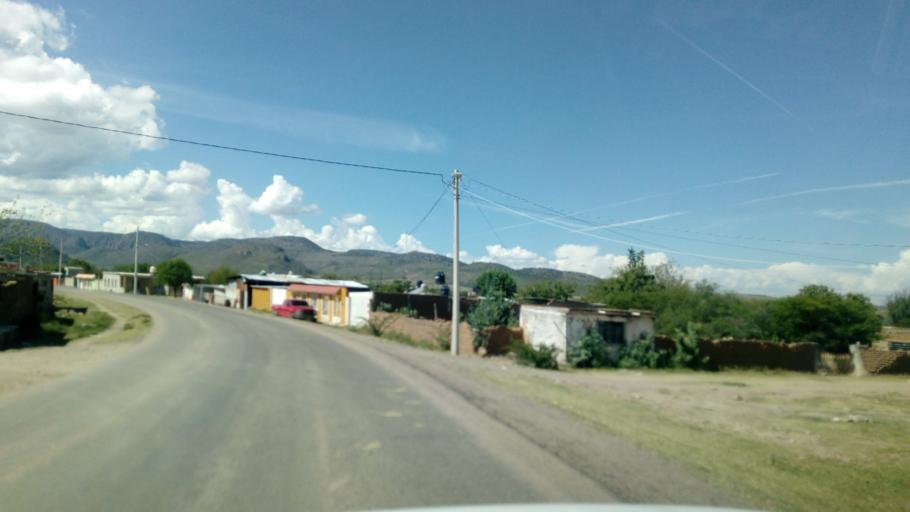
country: MX
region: Durango
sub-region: Durango
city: Jose Refugio Salcido
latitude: 23.8492
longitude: -104.4775
